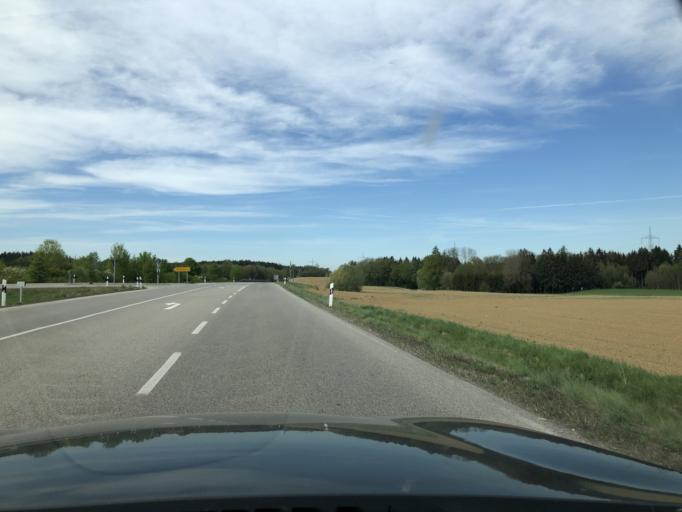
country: DE
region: Bavaria
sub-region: Swabia
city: Biberbach
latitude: 48.5232
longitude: 10.7935
